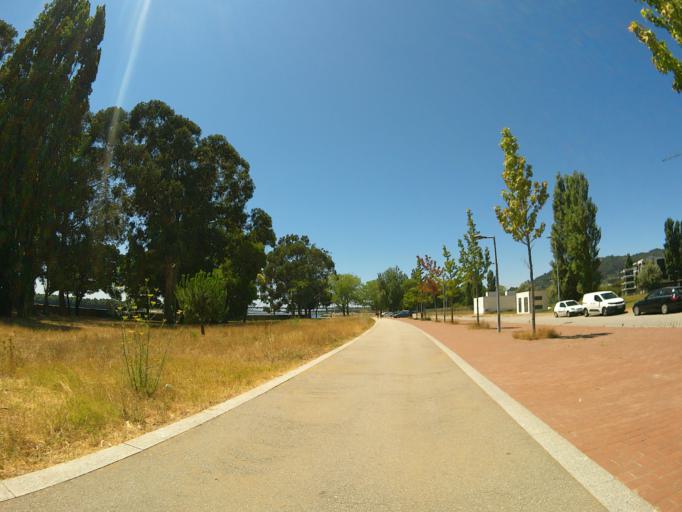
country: PT
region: Viana do Castelo
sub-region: Viana do Castelo
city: Meadela
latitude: 41.6969
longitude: -8.8108
